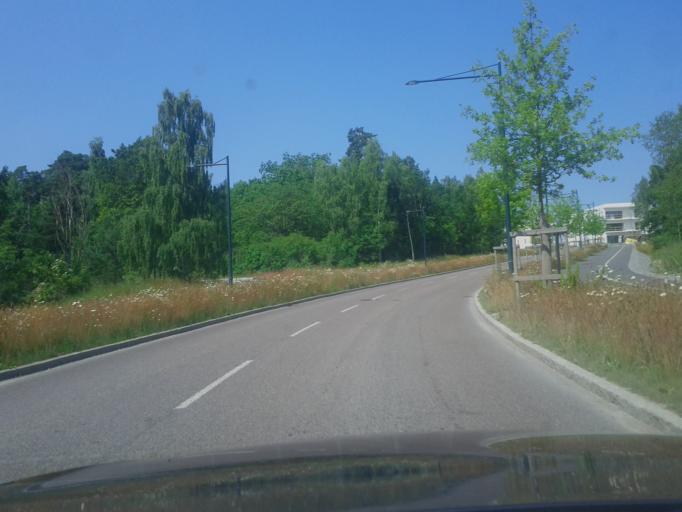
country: SE
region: Stockholm
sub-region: Taby Kommun
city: Taby
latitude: 59.4716
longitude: 18.1297
